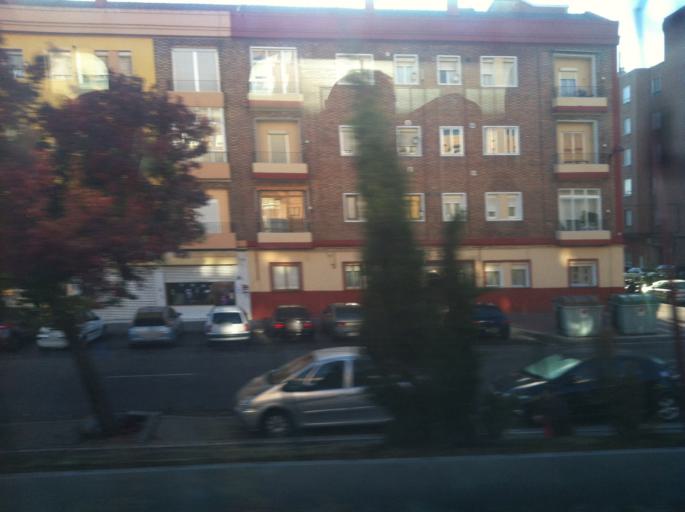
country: ES
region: Castille and Leon
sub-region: Provincia de Valladolid
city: Valladolid
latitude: 41.6493
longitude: -4.7112
